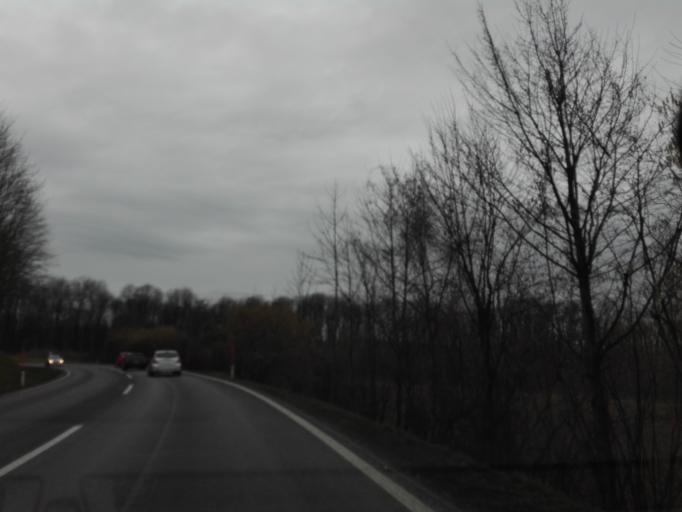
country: AT
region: Upper Austria
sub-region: Politischer Bezirk Linz-Land
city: Ansfelden
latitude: 48.2173
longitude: 14.2634
